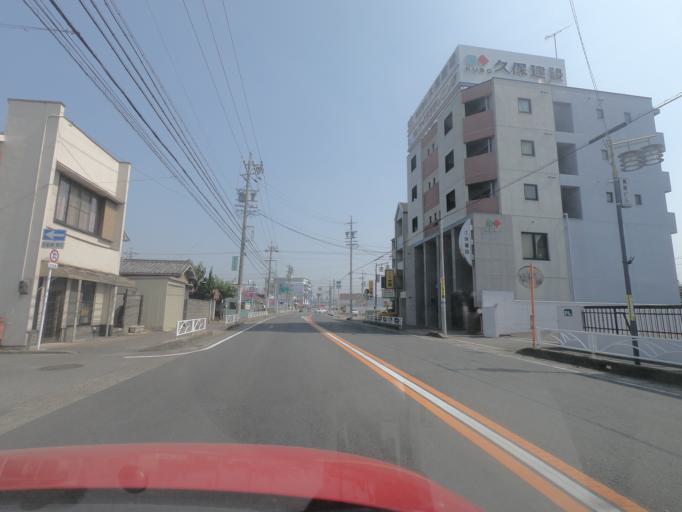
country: JP
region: Aichi
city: Kasugai
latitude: 35.2507
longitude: 136.9792
